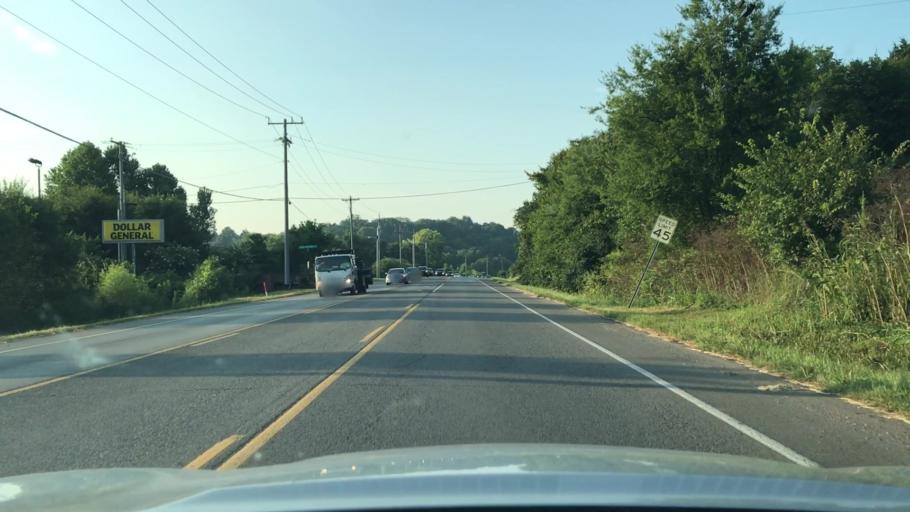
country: US
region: Tennessee
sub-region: Williamson County
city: Nolensville
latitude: 36.0117
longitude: -86.7031
